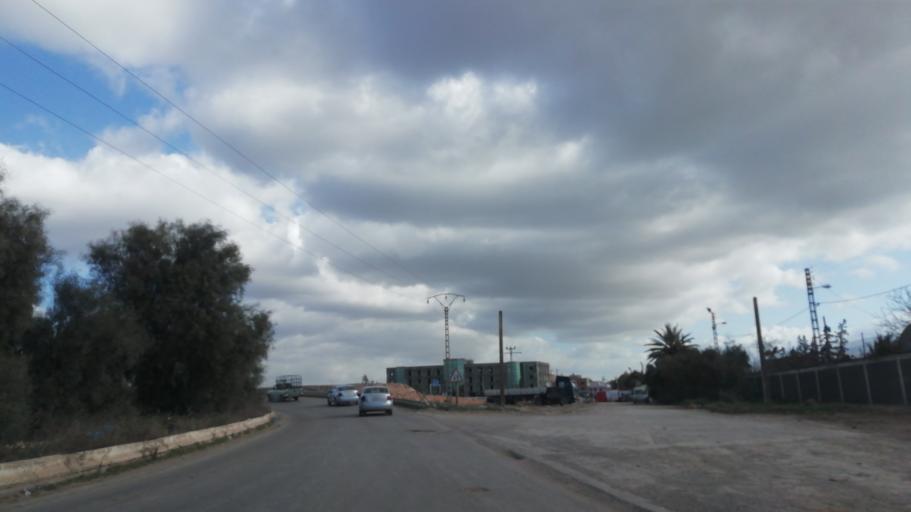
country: DZ
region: Oran
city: Es Senia
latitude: 35.6228
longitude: -0.5881
